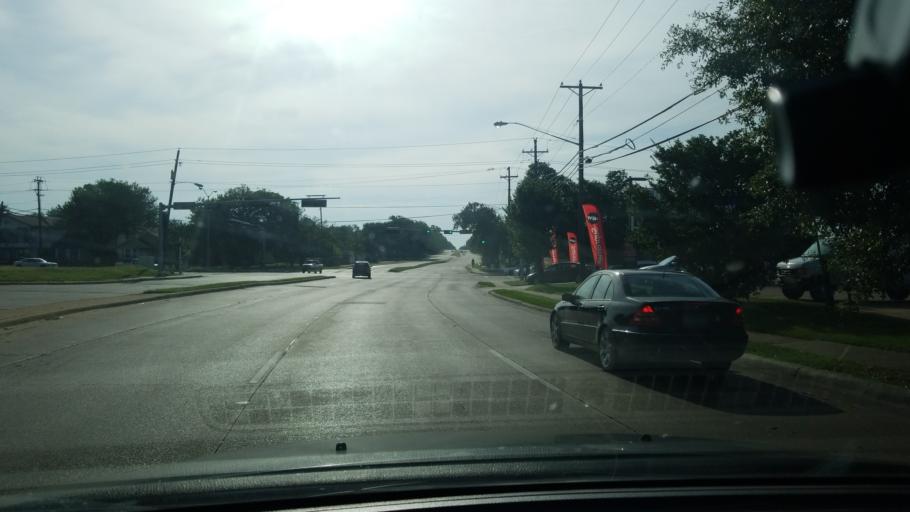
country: US
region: Texas
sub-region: Dallas County
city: Balch Springs
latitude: 32.7486
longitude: -96.6493
